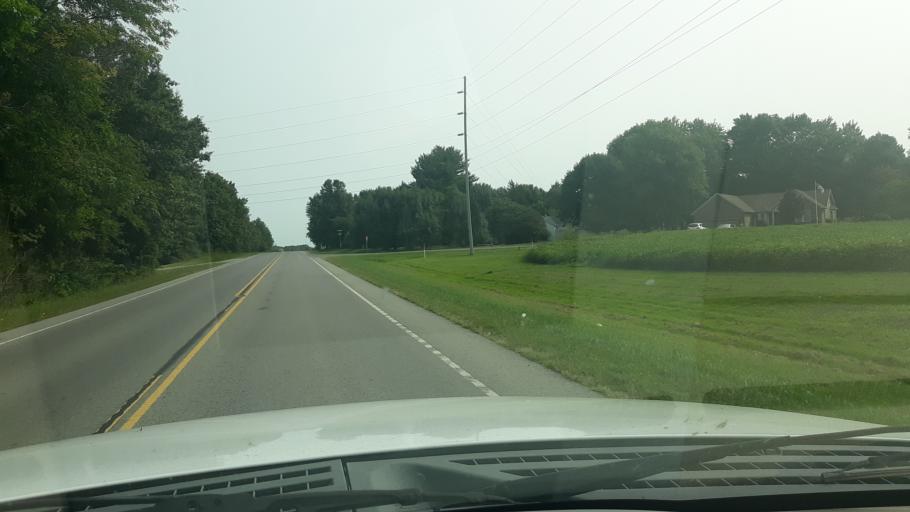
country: US
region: Illinois
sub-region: White County
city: Carmi
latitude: 38.0678
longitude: -88.2133
